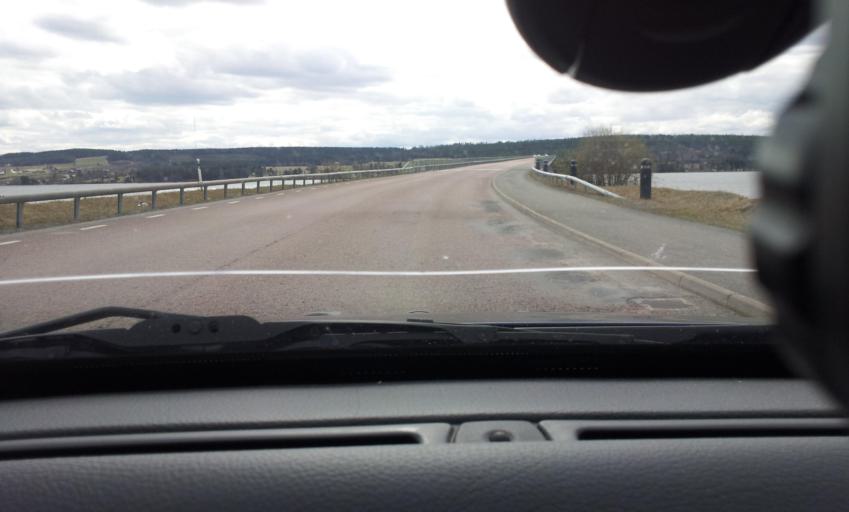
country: SE
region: Jaemtland
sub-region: OEstersunds Kommun
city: Ostersund
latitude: 63.1656
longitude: 14.6084
